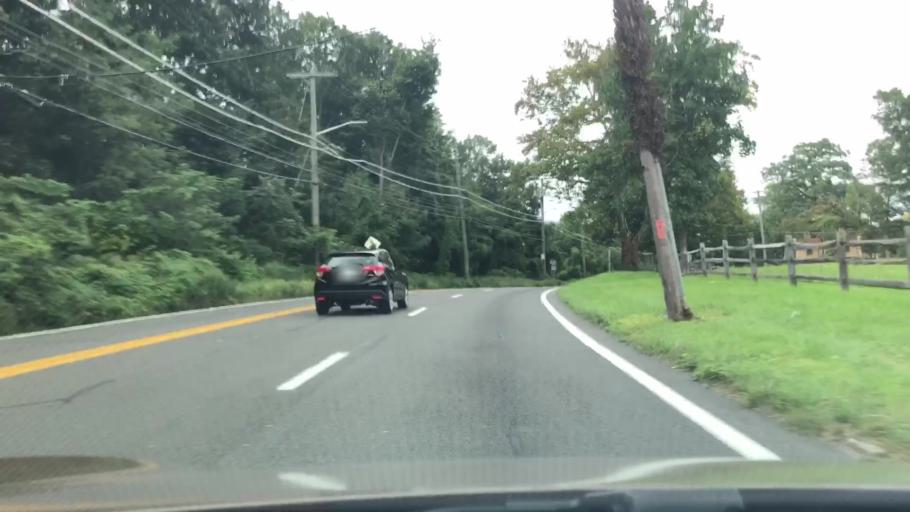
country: US
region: New York
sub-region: Westchester County
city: Sleepy Hollow
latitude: 41.1224
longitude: -73.8617
